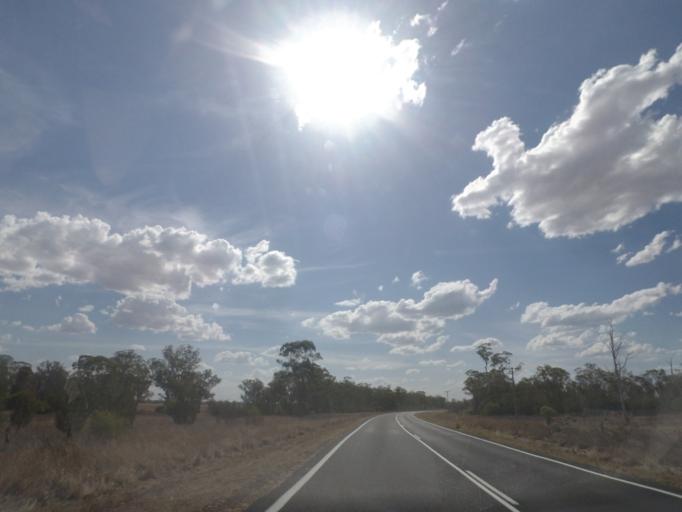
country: AU
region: New South Wales
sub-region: Moree Plains
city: Boggabilla
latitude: -28.4150
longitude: 151.1203
